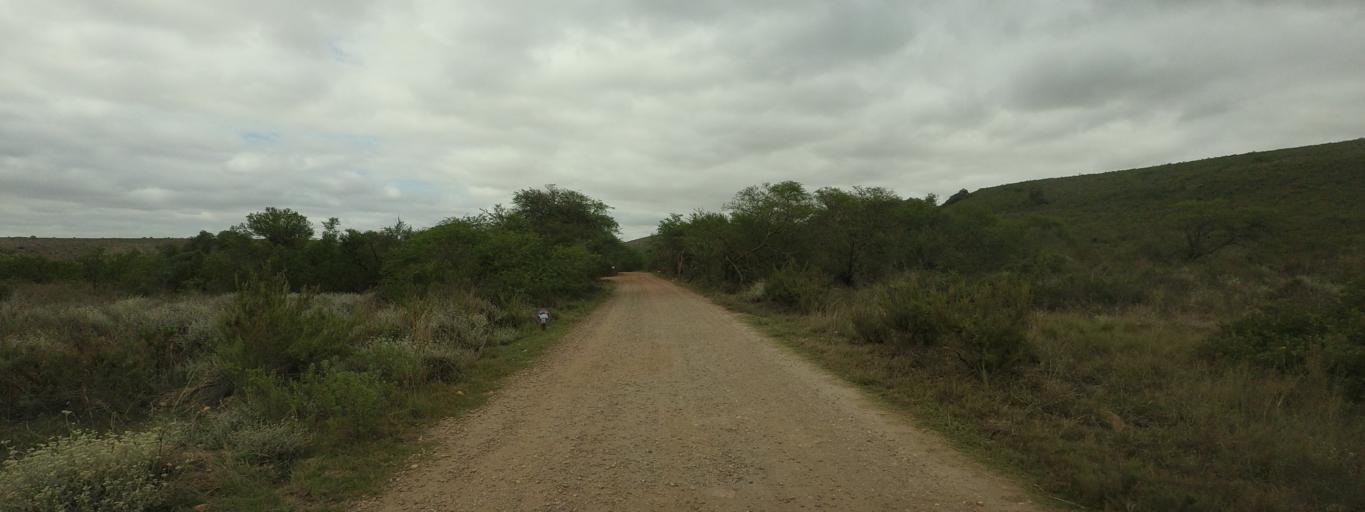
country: ZA
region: Western Cape
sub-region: Overberg District Municipality
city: Swellendam
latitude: -34.0662
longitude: 20.4369
